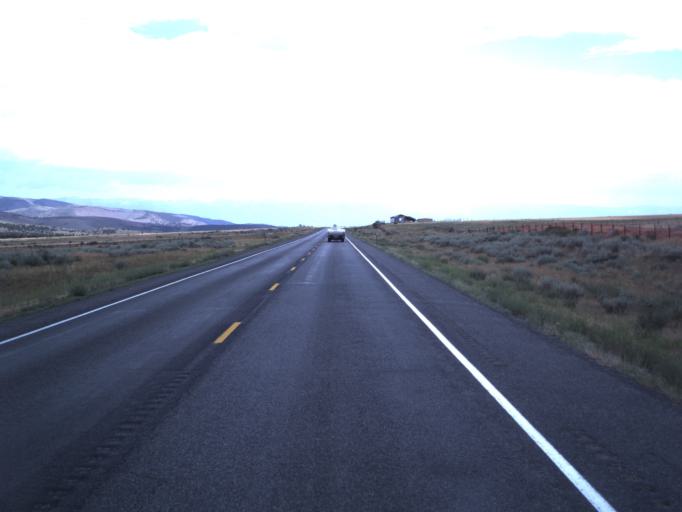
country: US
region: Utah
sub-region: Sanpete County
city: Fountain Green
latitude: 39.6816
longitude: -111.6736
